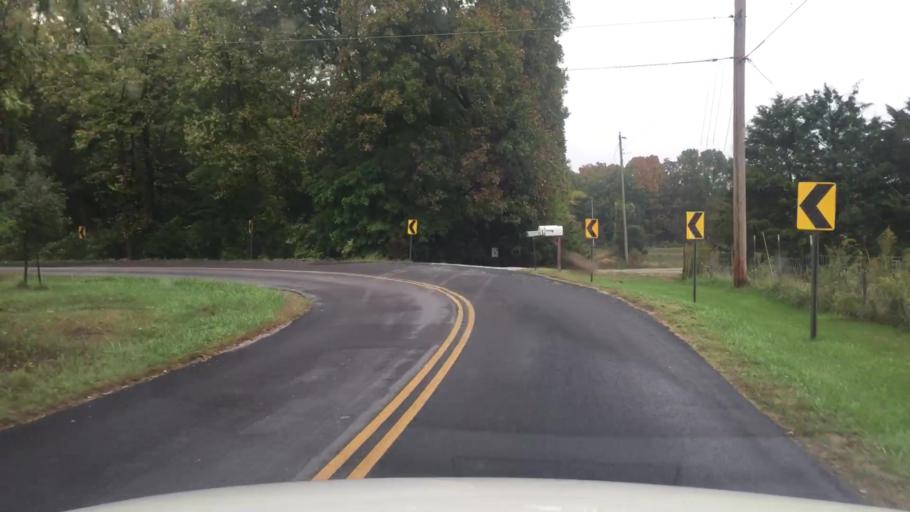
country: US
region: Missouri
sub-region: Boone County
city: Ashland
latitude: 38.8184
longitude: -92.2927
